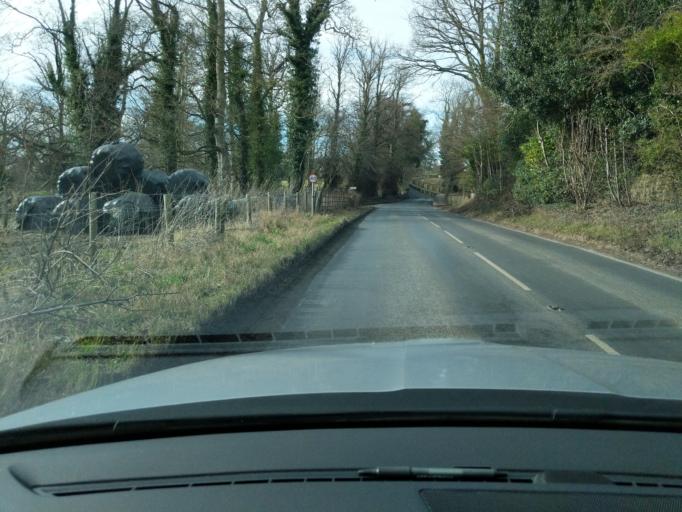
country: GB
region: England
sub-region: North Yorkshire
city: Catterick Garrison
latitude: 54.4033
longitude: -1.7190
